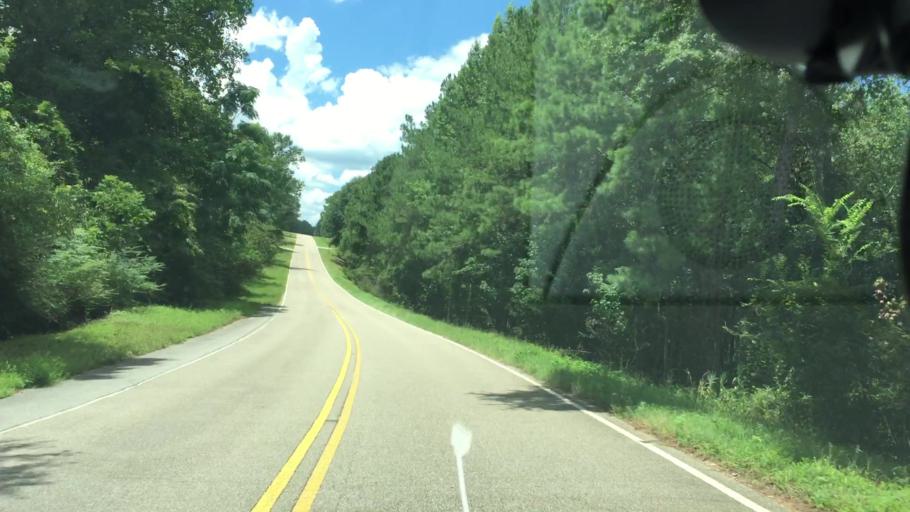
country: US
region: Alabama
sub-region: Coffee County
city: New Brockton
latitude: 31.4087
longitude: -85.8440
